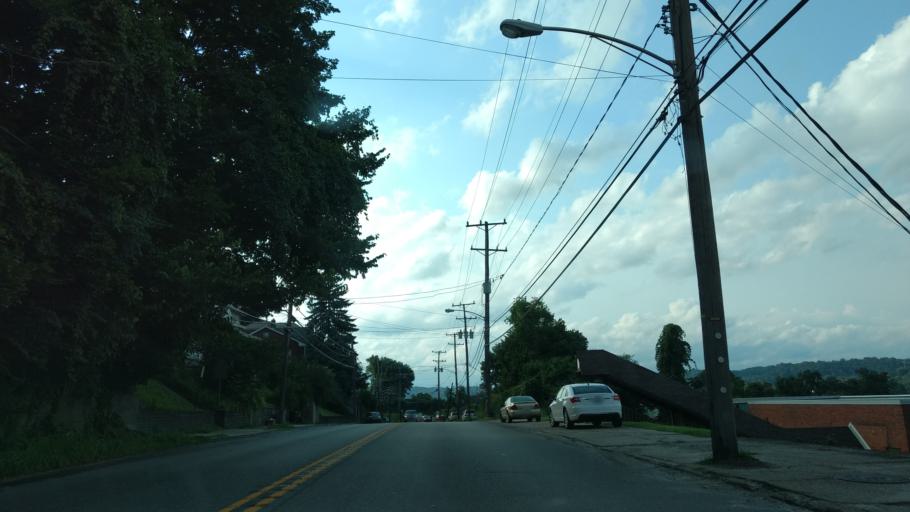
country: US
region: Pennsylvania
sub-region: Allegheny County
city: McKees Rocks
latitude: 40.4821
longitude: -80.0697
